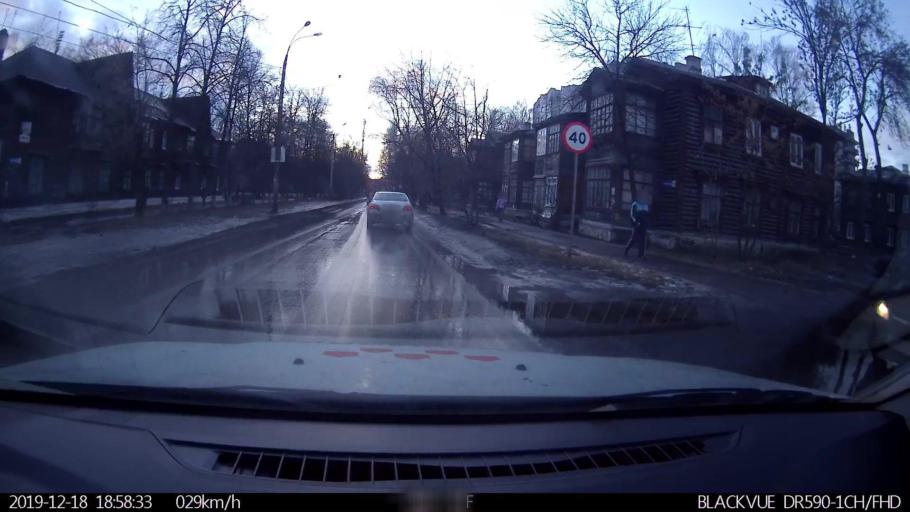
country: RU
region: Nizjnij Novgorod
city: Gorbatovka
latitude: 56.3351
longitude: 43.8398
